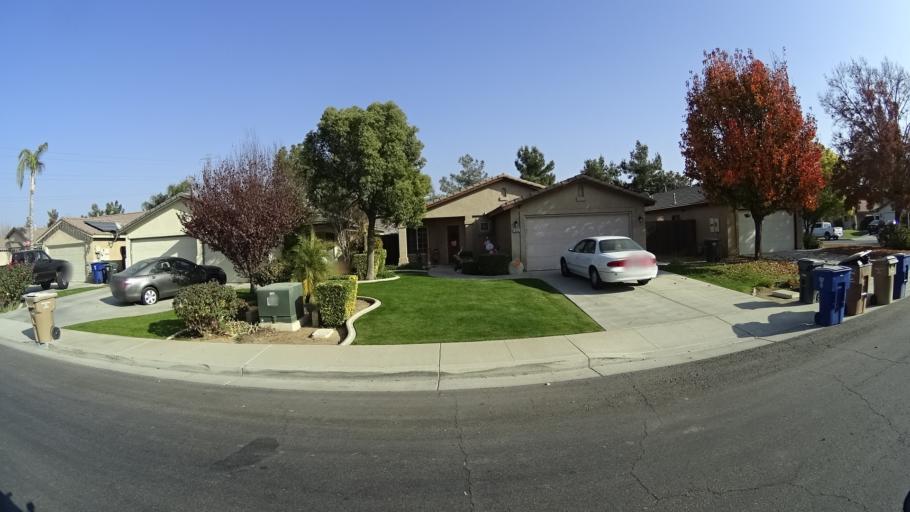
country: US
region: California
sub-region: Kern County
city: Greenacres
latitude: 35.3965
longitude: -119.0673
